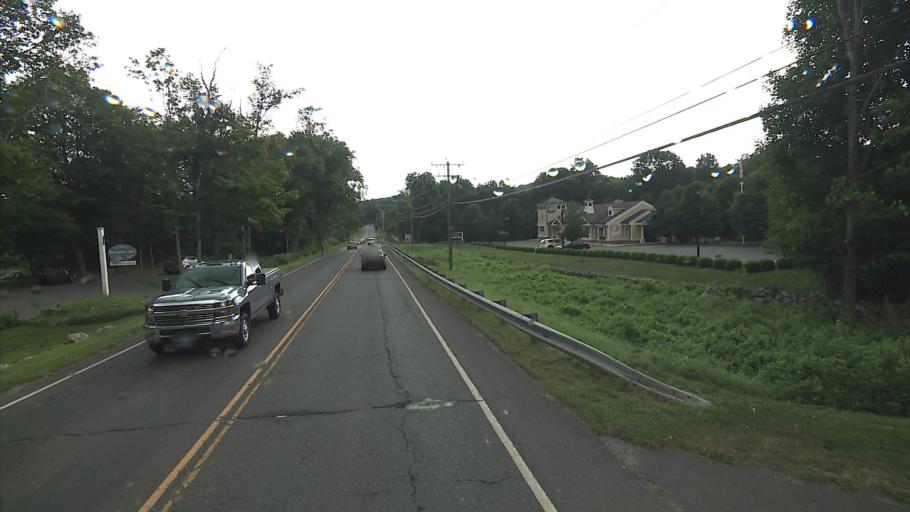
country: US
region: Connecticut
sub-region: New Haven County
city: Oxford
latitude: 41.4630
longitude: -73.1600
